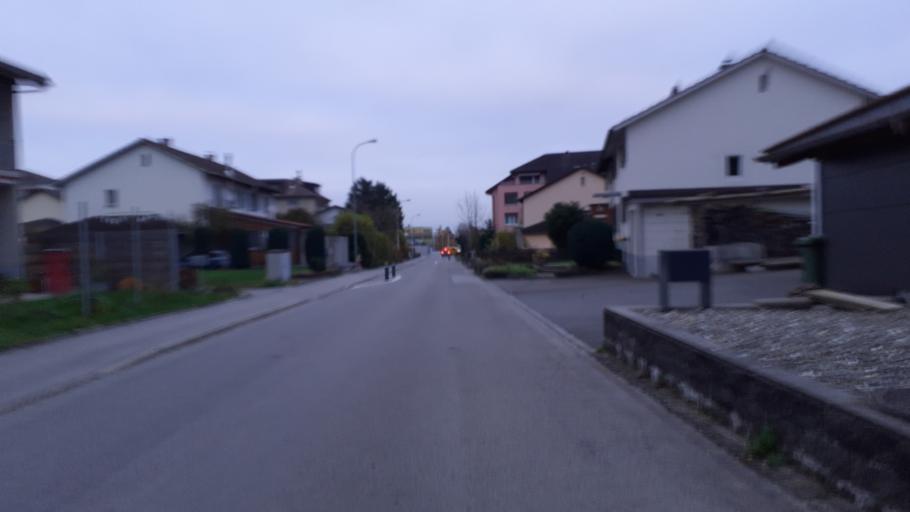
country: CH
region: Saint Gallen
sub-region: Wahlkreis Rheintal
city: Altstatten
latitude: 47.3795
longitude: 9.5529
